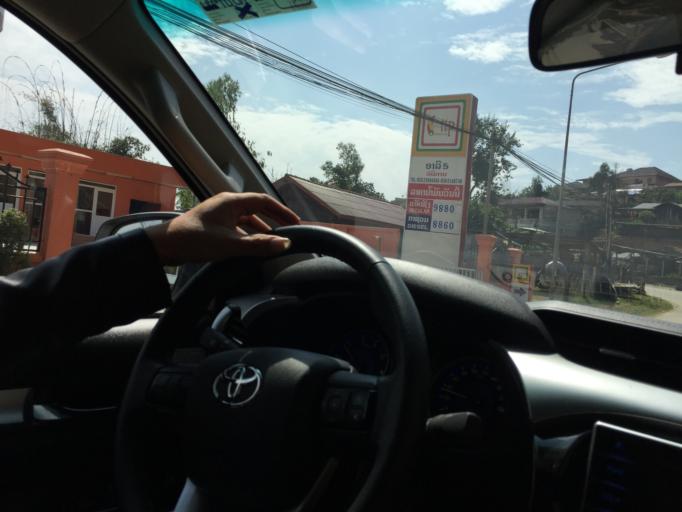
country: LA
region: Phongsali
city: Phongsali
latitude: 21.6809
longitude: 102.0969
